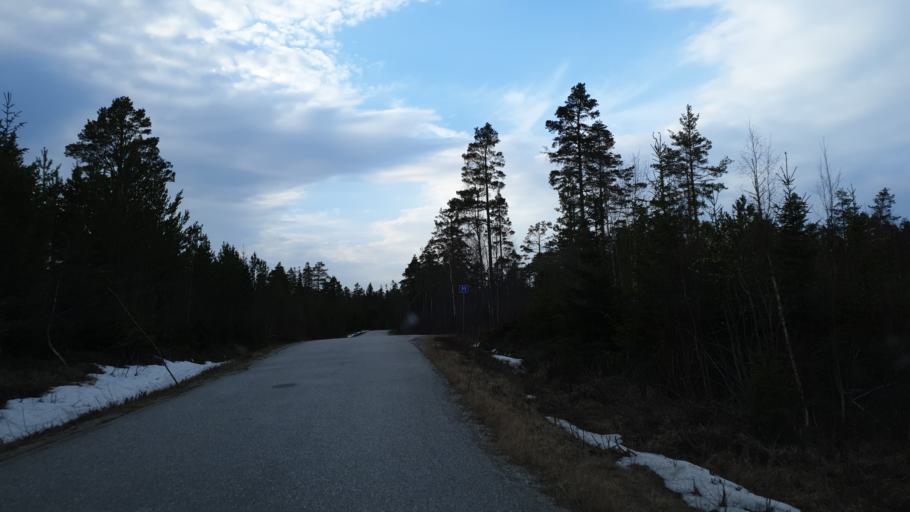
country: SE
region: Vaesternorrland
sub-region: Sundsvalls Kommun
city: Njurundabommen
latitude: 62.0247
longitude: 17.4052
